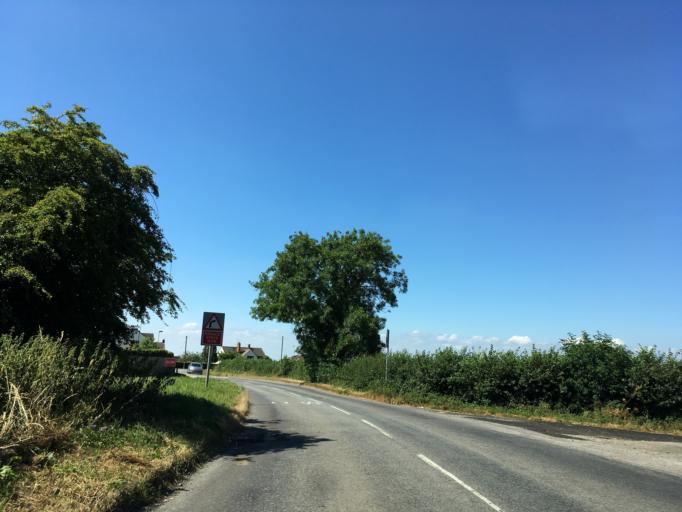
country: GB
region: England
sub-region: South Gloucestershire
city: Chipping Sodbury
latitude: 51.5295
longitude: -2.3959
